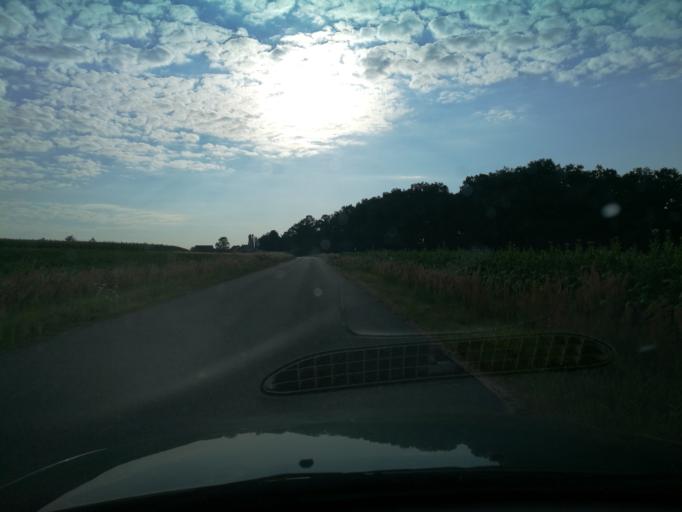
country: DE
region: Bavaria
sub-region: Regierungsbezirk Mittelfranken
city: Obermichelbach
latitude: 49.5089
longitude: 10.9487
